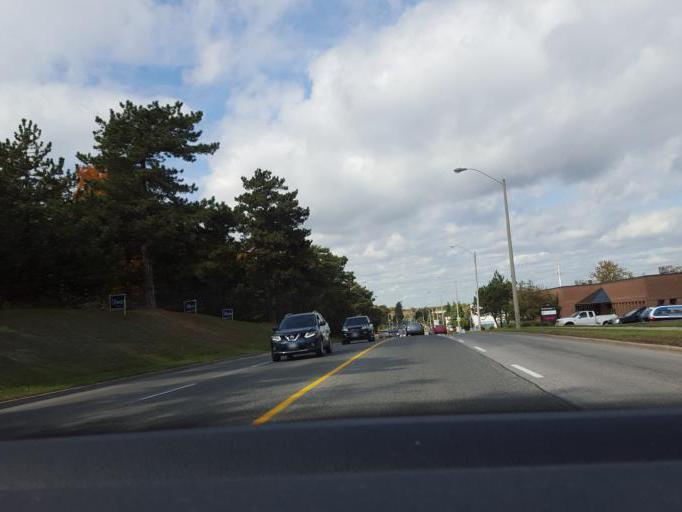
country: CA
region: Ontario
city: Scarborough
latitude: 43.8045
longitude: -79.2005
